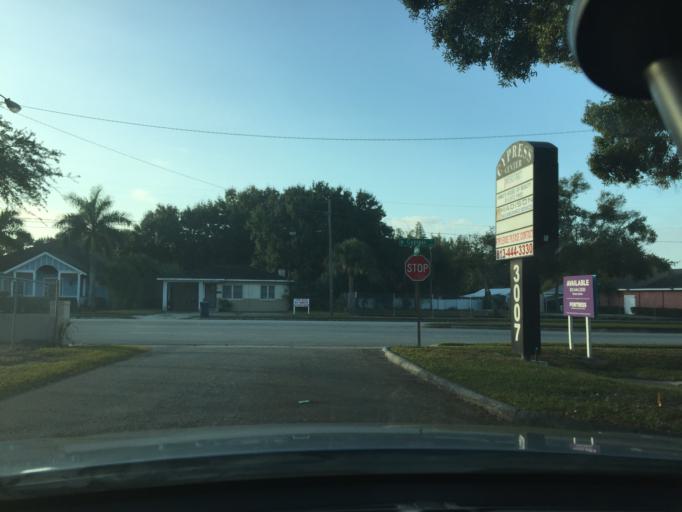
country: US
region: Florida
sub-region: Hillsborough County
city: Tampa
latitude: 27.9524
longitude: -82.4920
